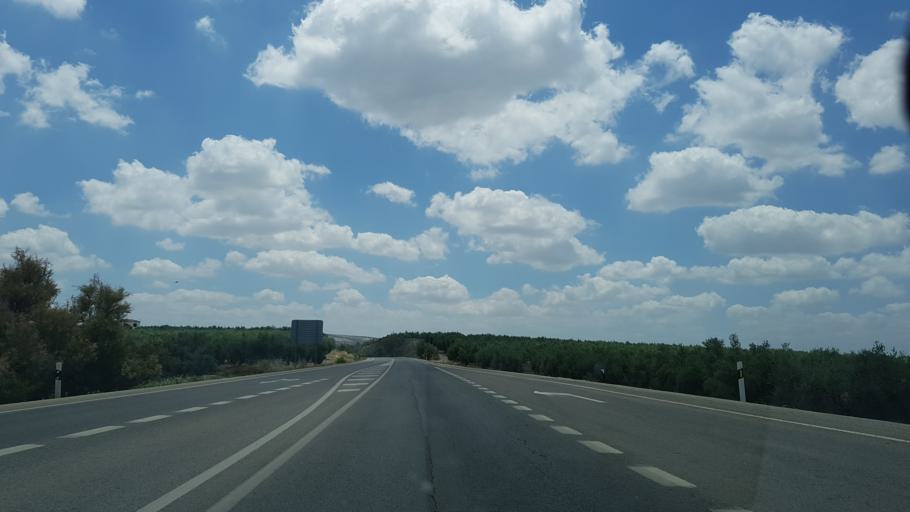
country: ES
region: Andalusia
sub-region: Province of Cordoba
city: Cabra
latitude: 37.4810
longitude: -4.4622
